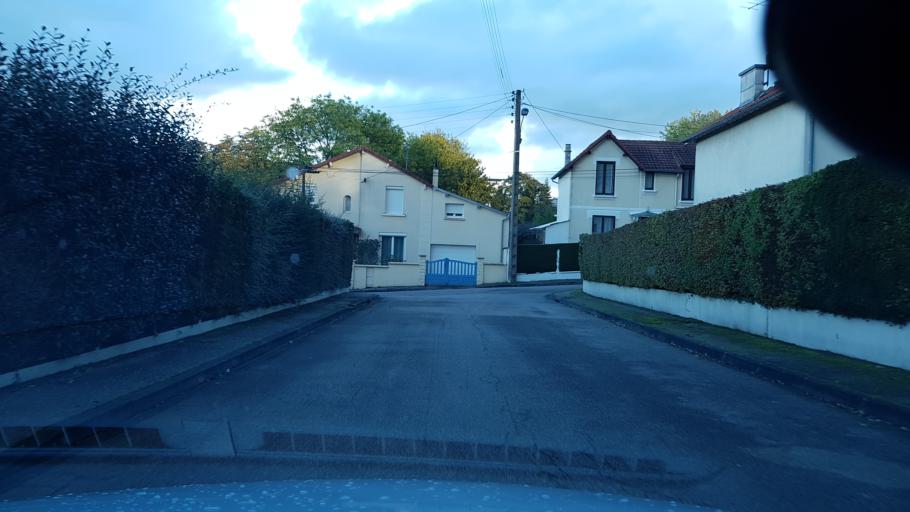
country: FR
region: Haute-Normandie
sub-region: Departement de l'Eure
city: Evreux
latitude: 49.0158
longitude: 1.1283
